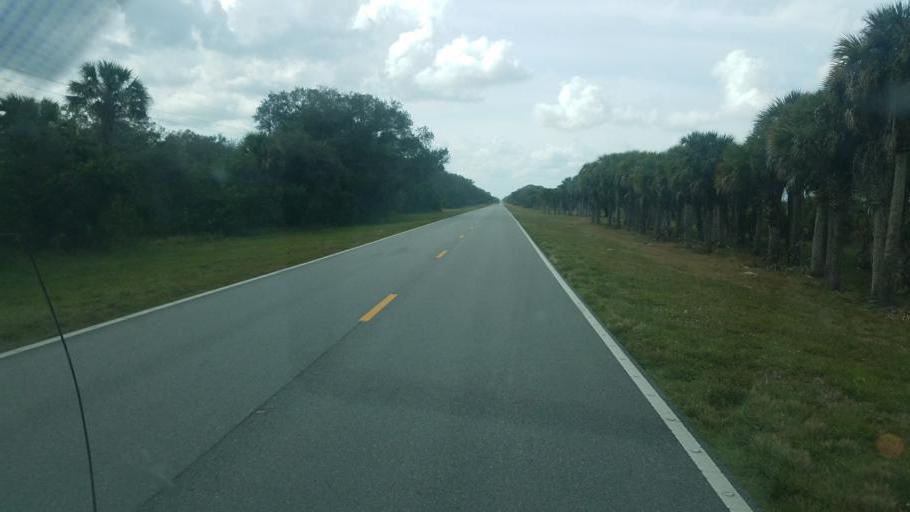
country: US
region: Florida
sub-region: Okeechobee County
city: Cypress Quarters
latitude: 27.4501
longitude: -80.6961
